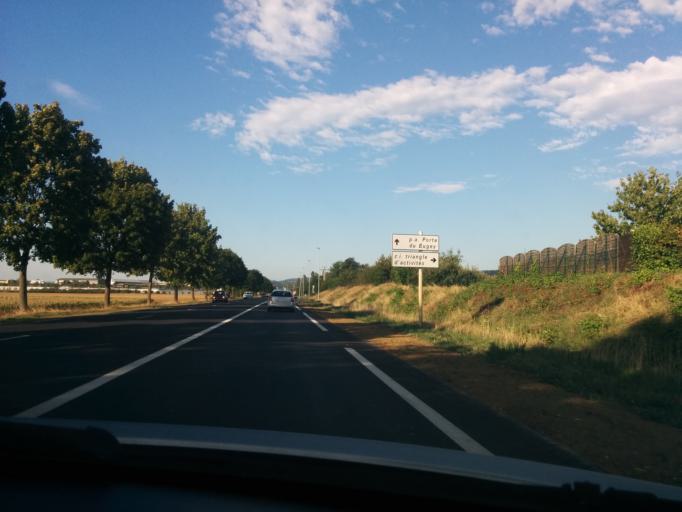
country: FR
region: Rhone-Alpes
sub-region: Departement de l'Ain
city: Amberieu-en-Bugey
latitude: 45.9625
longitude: 5.3322
